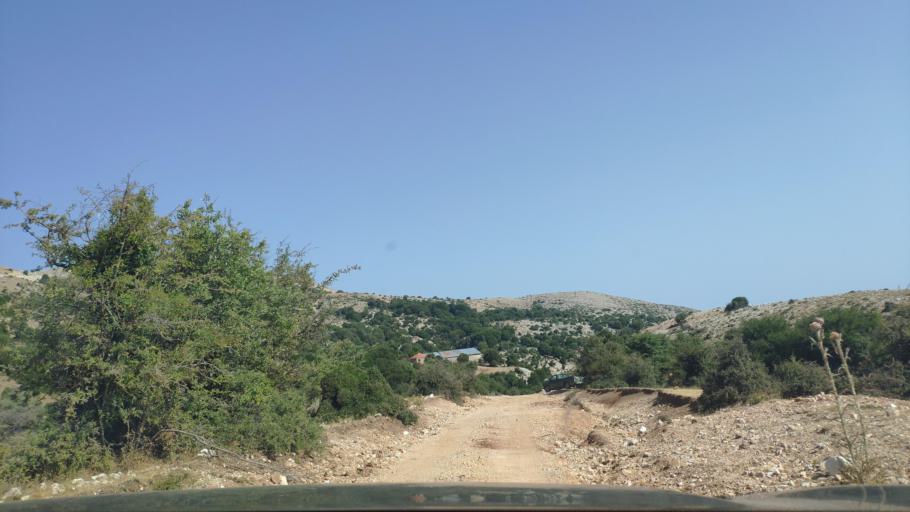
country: GR
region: West Greece
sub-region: Nomos Aitolias kai Akarnanias
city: Monastirakion
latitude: 38.7992
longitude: 20.9974
